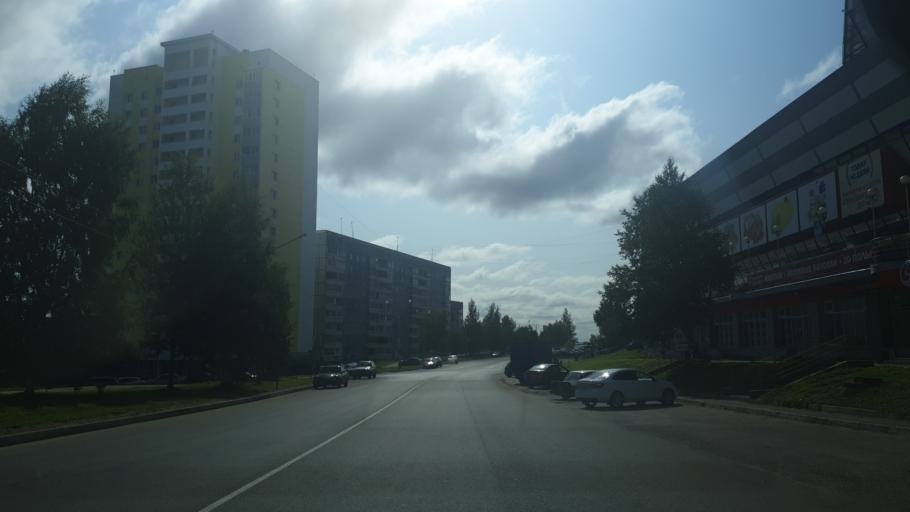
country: RU
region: Komi Republic
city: Ezhva
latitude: 61.7857
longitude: 50.7567
